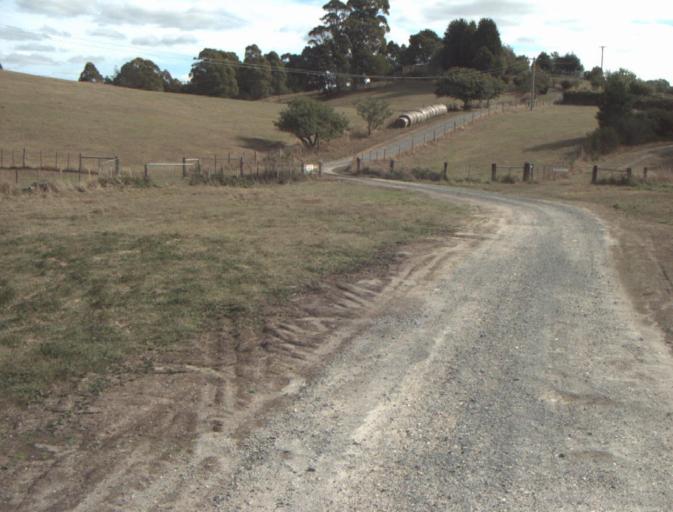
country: AU
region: Tasmania
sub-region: Launceston
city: Mayfield
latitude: -41.1970
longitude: 147.1943
